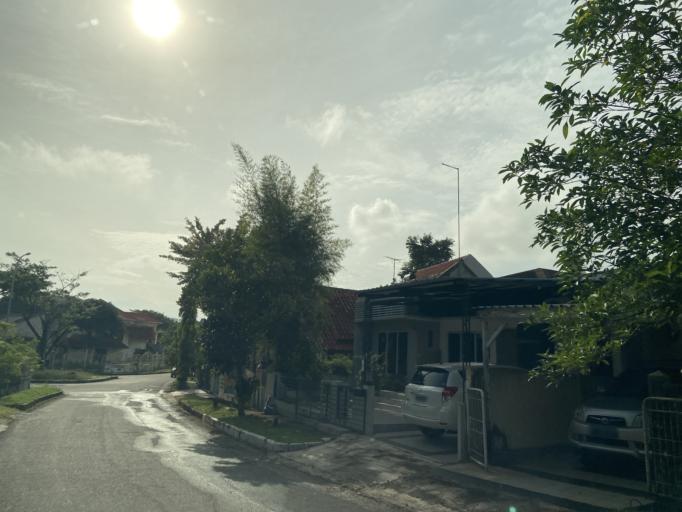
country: SG
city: Singapore
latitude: 1.1118
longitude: 104.0221
